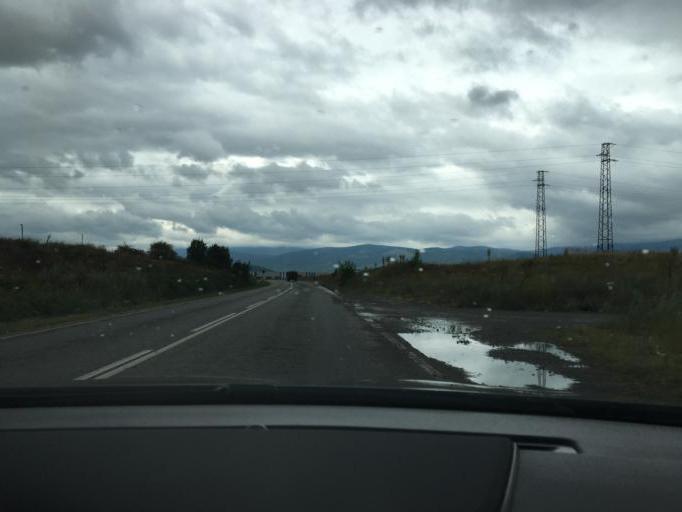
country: BG
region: Kyustendil
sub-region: Obshtina Kyustendil
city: Kyustendil
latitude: 42.2867
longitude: 22.7210
